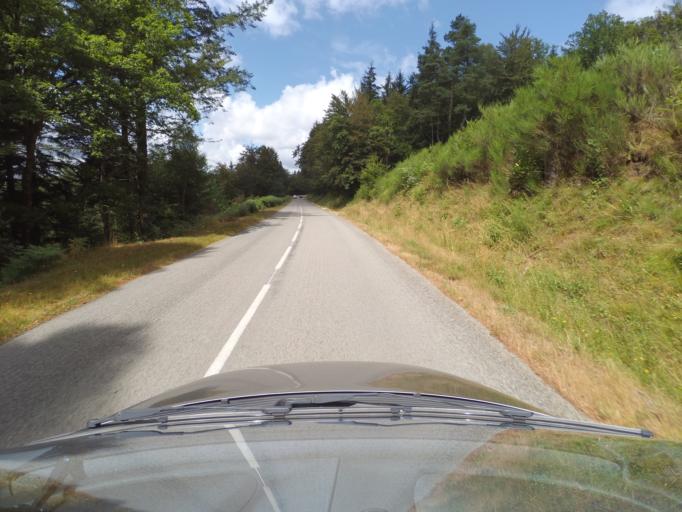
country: FR
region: Limousin
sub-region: Departement de la Creuse
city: Bourganeuf
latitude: 45.9056
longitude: 1.8591
